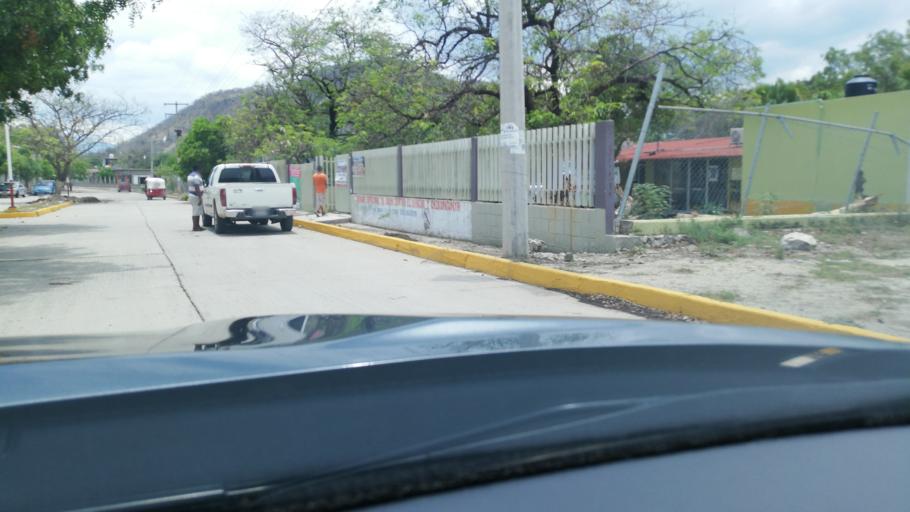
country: MX
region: Oaxaca
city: Santa Maria Jalapa del Marques
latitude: 16.4449
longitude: -95.4426
